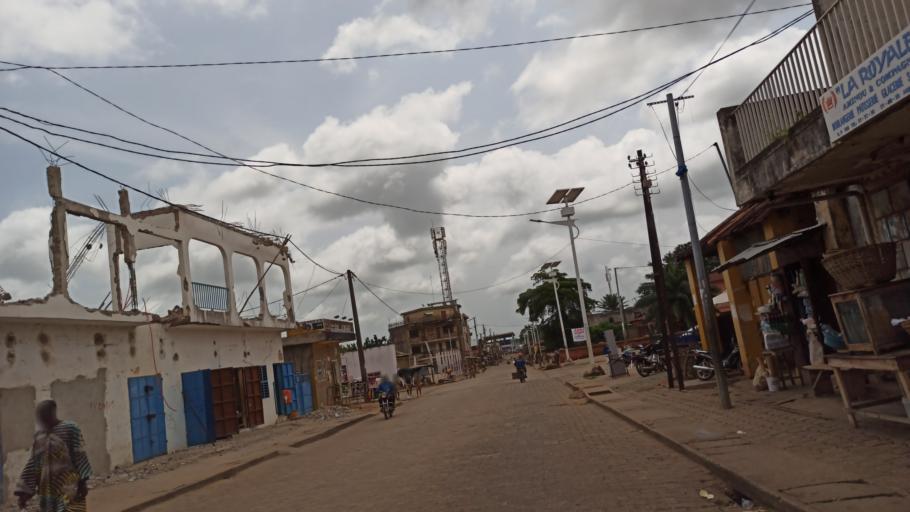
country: BJ
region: Queme
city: Porto-Novo
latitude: 6.4702
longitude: 2.6258
